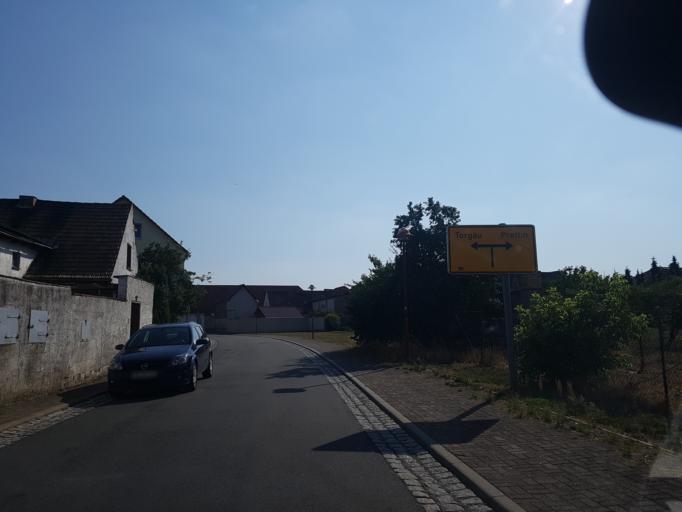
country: DE
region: Saxony-Anhalt
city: Prettin
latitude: 51.6473
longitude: 12.9830
